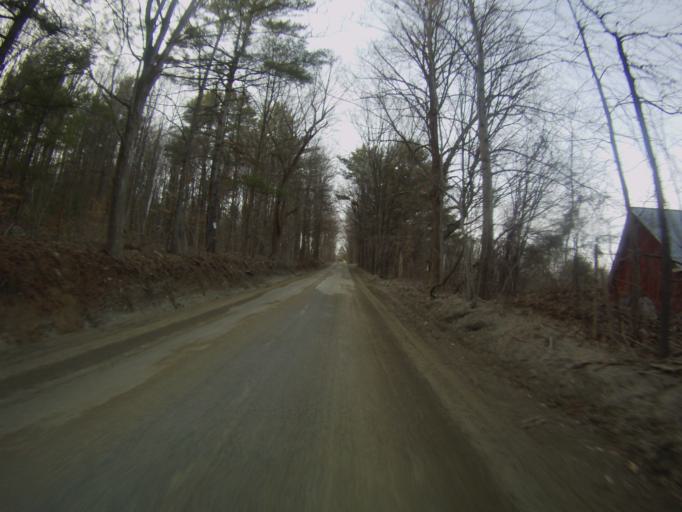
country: US
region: Vermont
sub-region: Addison County
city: Middlebury (village)
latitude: 44.0232
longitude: -73.2589
